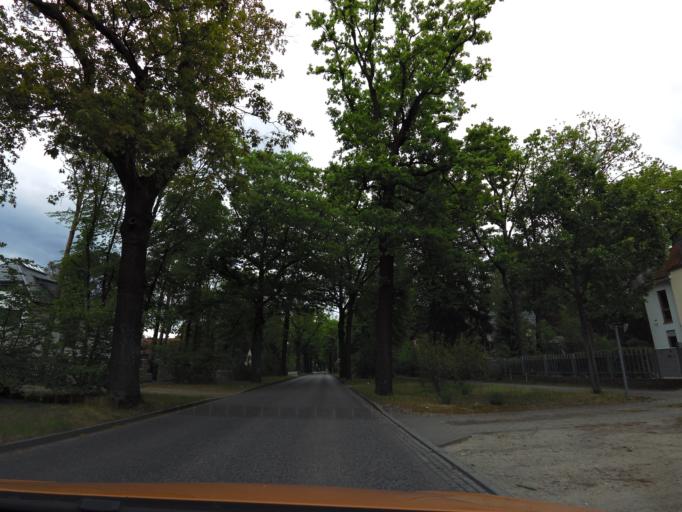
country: DE
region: Brandenburg
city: Kleinmachnow
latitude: 52.4106
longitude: 13.2394
